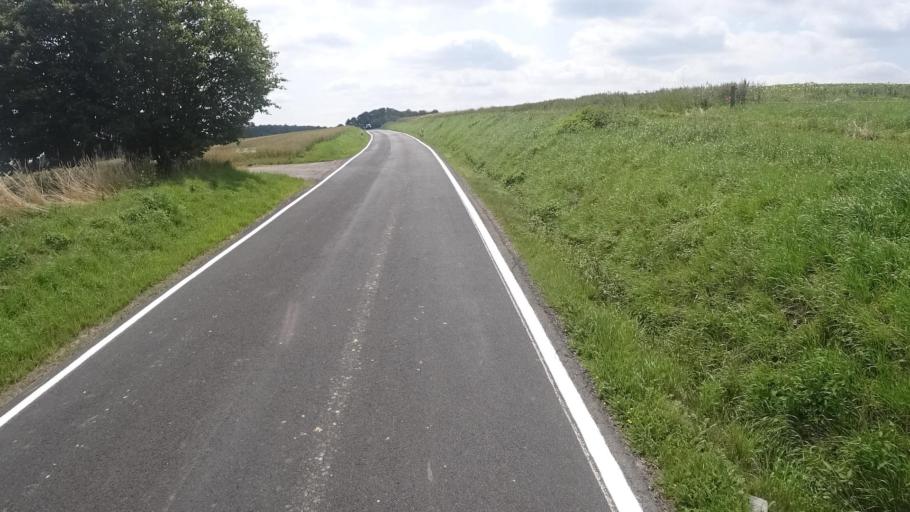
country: DE
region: Rheinland-Pfalz
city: Vettelschoss
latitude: 50.5895
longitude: 7.3555
